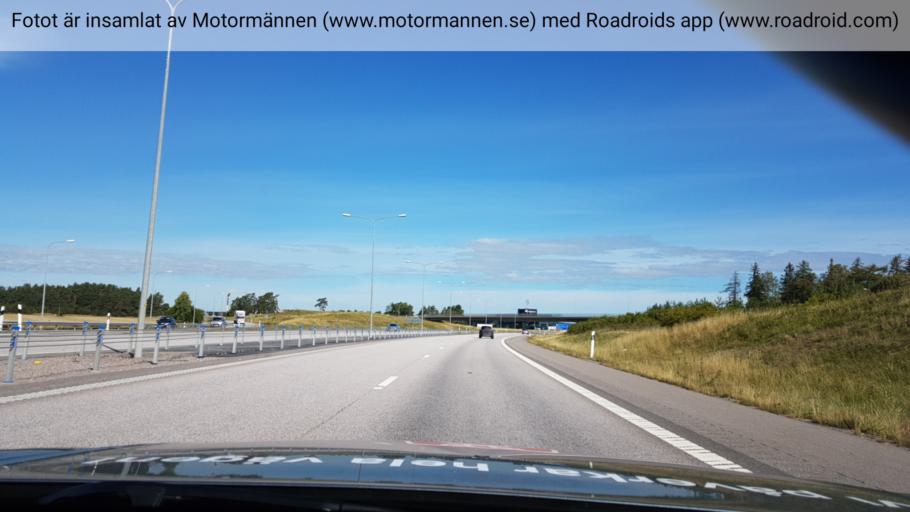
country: SE
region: Uppsala
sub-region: Uppsala Kommun
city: Saevja
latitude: 59.8383
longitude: 17.7335
